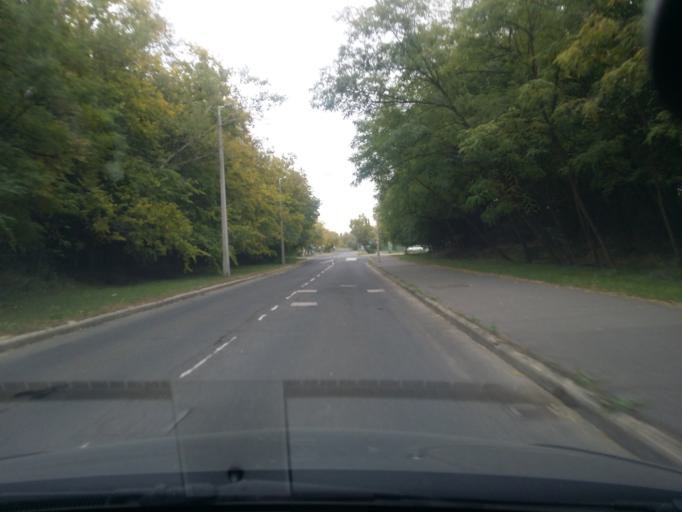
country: HU
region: Budapest
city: Budapest XV. keruelet
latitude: 47.5911
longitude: 19.1153
